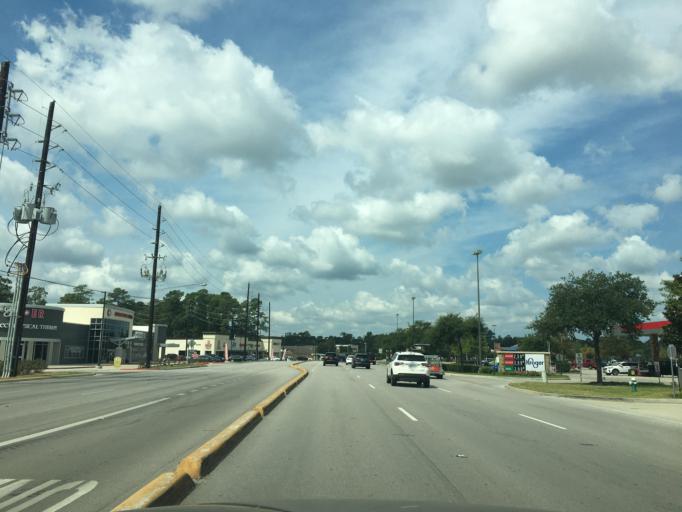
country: US
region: Texas
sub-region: Harris County
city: Spring
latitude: 30.1230
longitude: -95.4059
